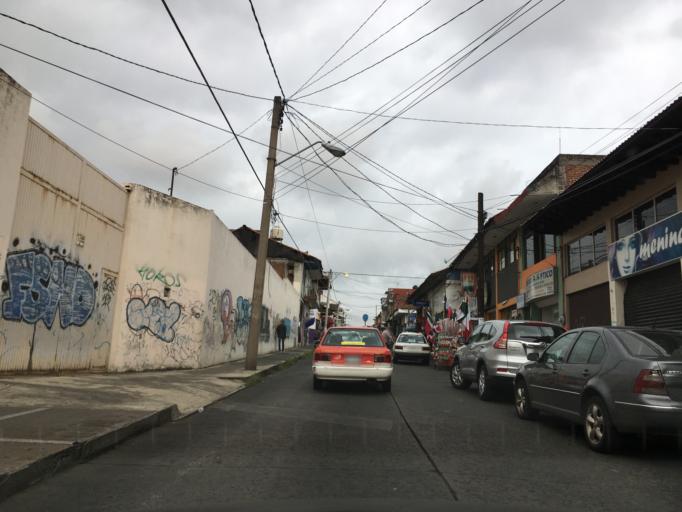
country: MX
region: Michoacan
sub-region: Uruapan
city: Uruapan
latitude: 19.4194
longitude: -102.0583
